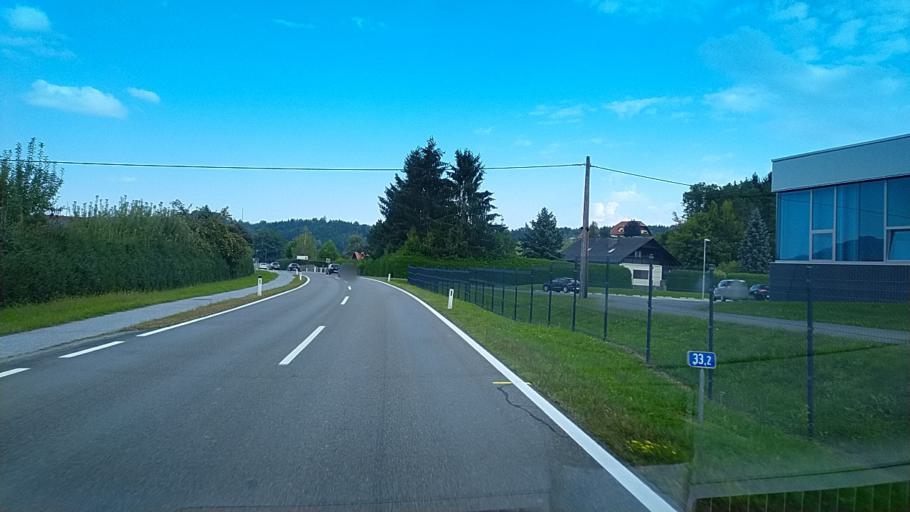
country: AT
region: Styria
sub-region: Politischer Bezirk Deutschlandsberg
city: Schwanberg
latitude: 46.7531
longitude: 15.2182
